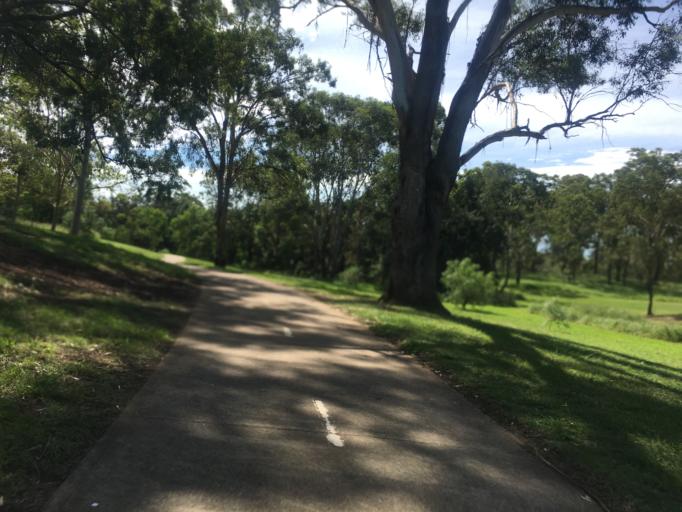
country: AU
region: New South Wales
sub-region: Camden
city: Camden South
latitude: -34.0810
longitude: 150.6998
